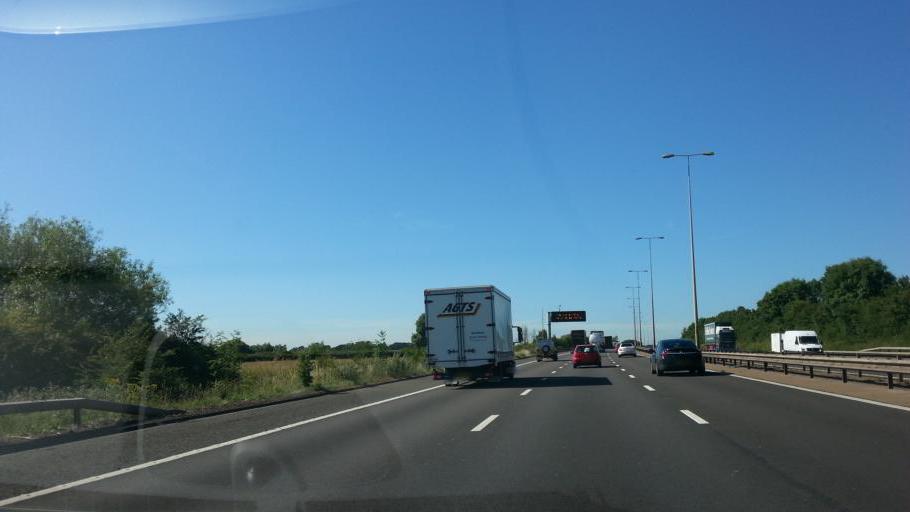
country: GB
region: England
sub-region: Worcestershire
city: Worcester
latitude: 52.1811
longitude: -2.1720
